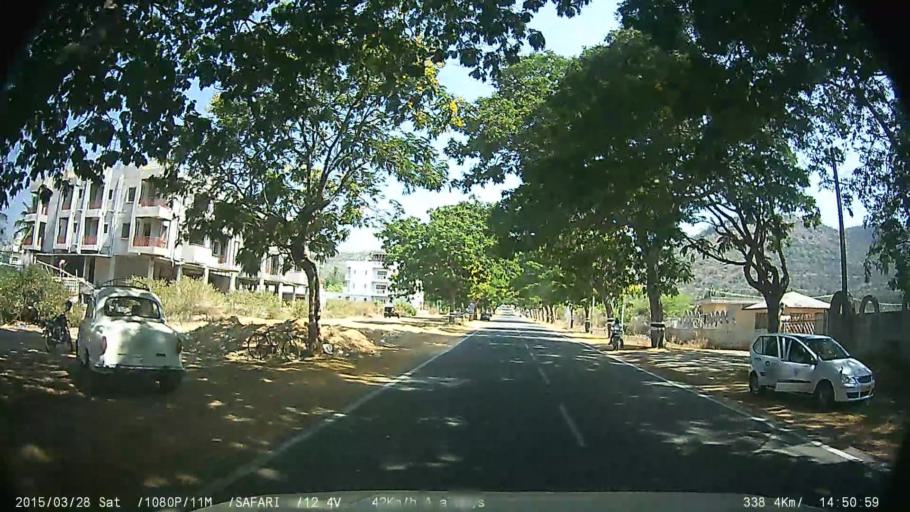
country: IN
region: Karnataka
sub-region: Mysore
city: Mysore
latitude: 12.2926
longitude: 76.6830
